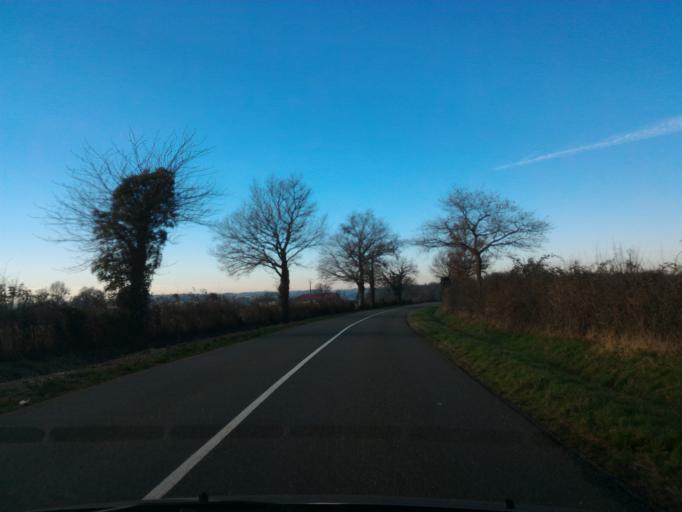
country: FR
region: Poitou-Charentes
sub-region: Departement de la Charente
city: Loubert
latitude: 46.0291
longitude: 0.5320
